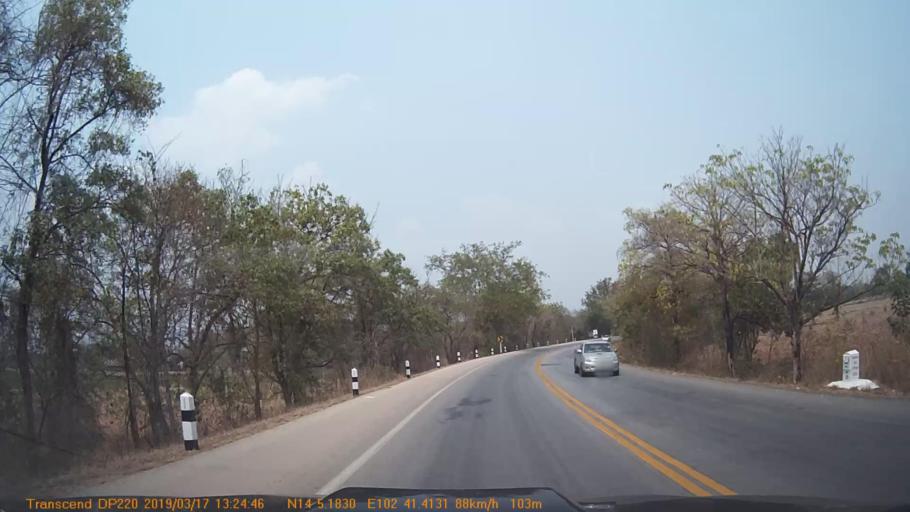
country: TH
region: Sa Kaeo
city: Ta Phraya
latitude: 14.0867
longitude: 102.6904
